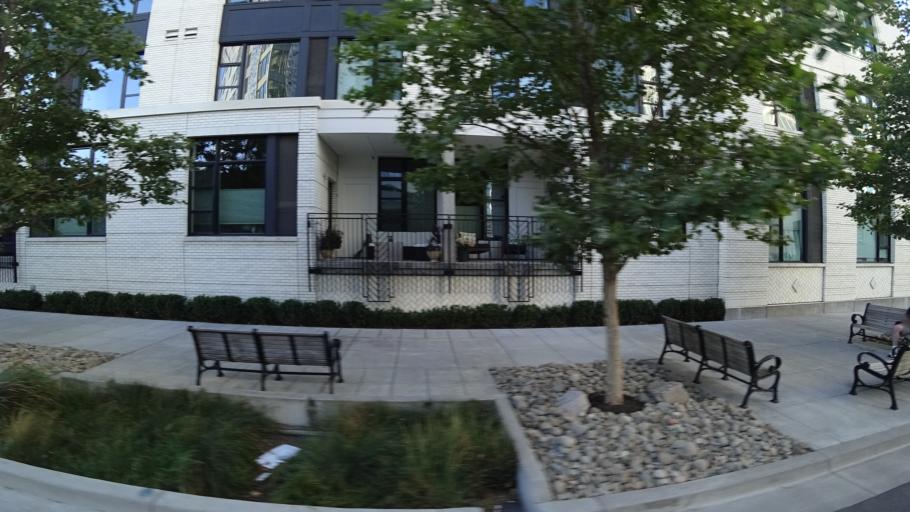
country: US
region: Oregon
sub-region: Multnomah County
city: Portland
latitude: 45.5329
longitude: -122.6837
